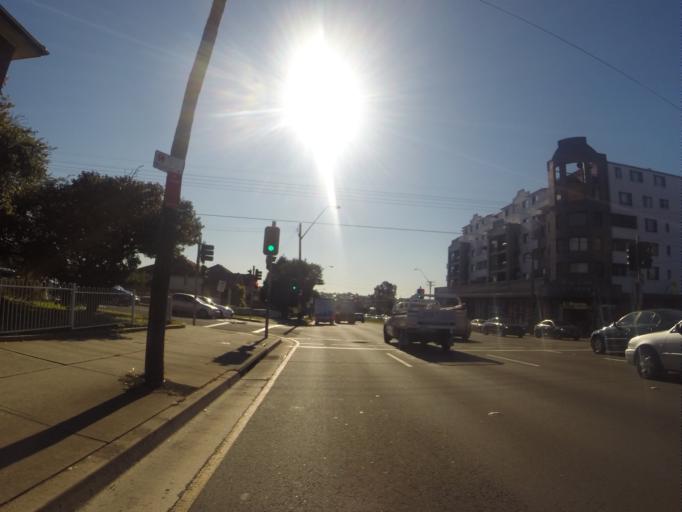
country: AU
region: New South Wales
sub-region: Canterbury
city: Lakemba
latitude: -33.9215
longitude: 151.0675
